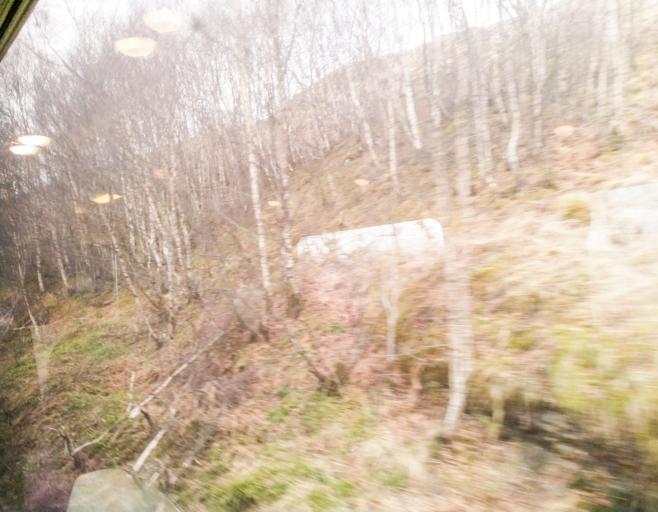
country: GB
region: Scotland
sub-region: Highland
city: Spean Bridge
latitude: 56.7859
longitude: -4.7313
